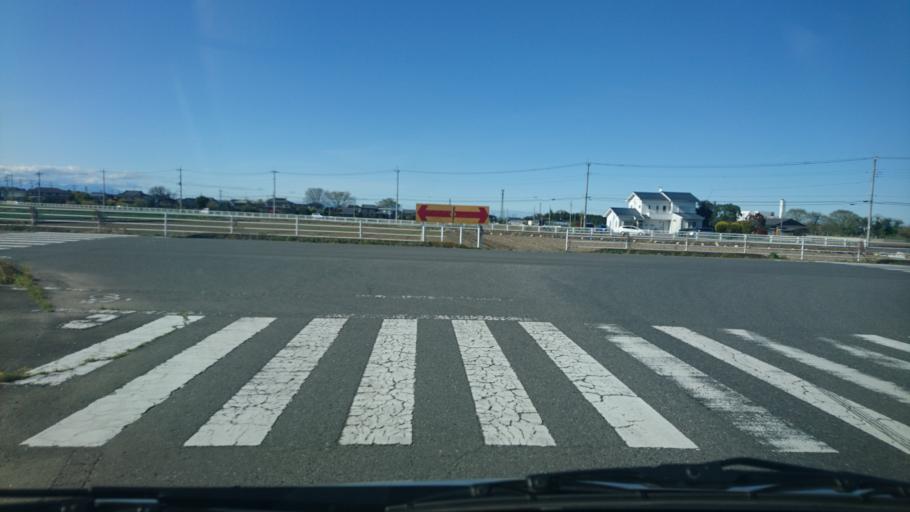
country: JP
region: Ibaraki
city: Yuki
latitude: 36.2812
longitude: 139.8992
